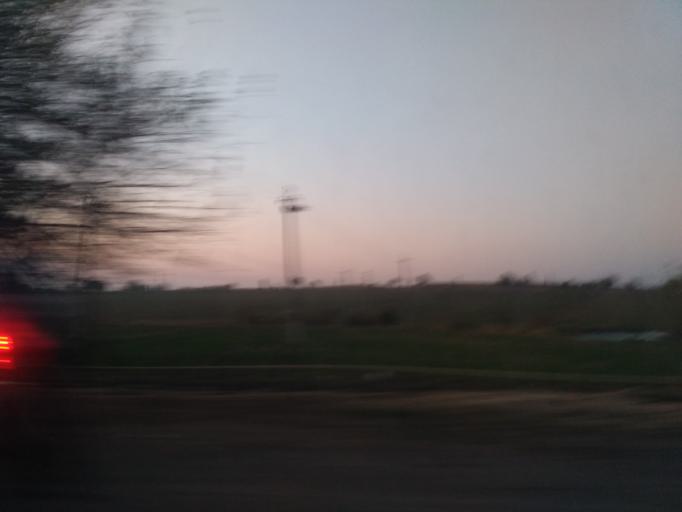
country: UZ
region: Toshkent
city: Salor
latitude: 41.4311
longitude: 69.3928
